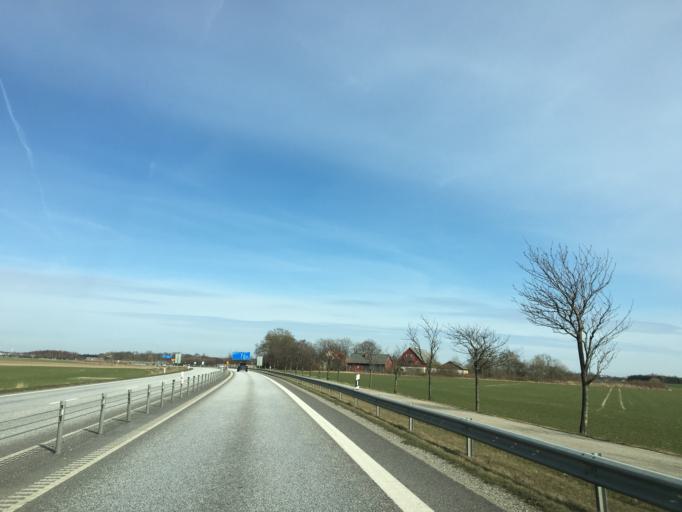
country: SE
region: Skane
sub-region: Staffanstorps Kommun
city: Hjaerup
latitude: 55.6917
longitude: 13.1250
